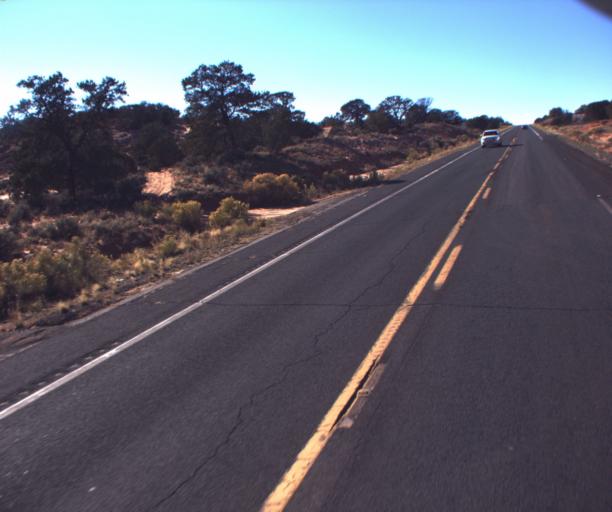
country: US
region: Arizona
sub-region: Coconino County
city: Kaibito
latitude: 36.5814
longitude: -110.7991
